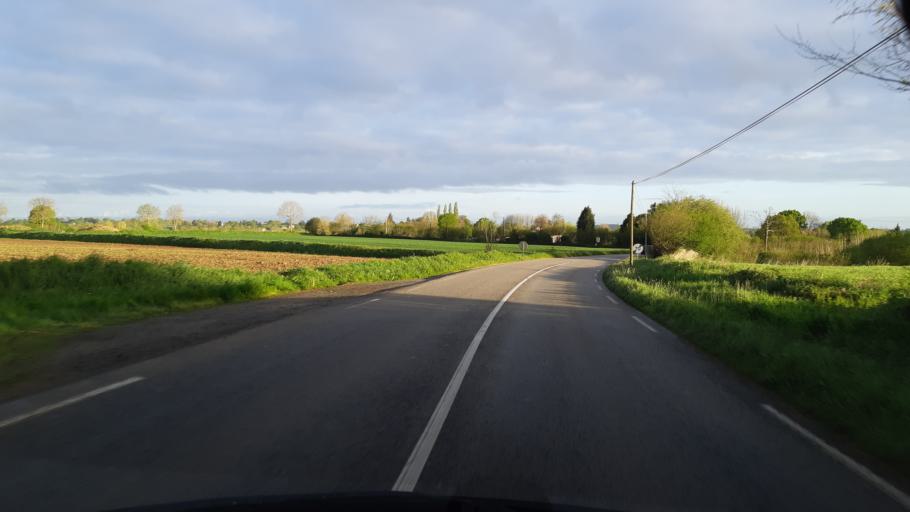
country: FR
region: Lower Normandy
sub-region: Departement de la Manche
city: Agneaux
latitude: 49.0544
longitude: -1.1317
